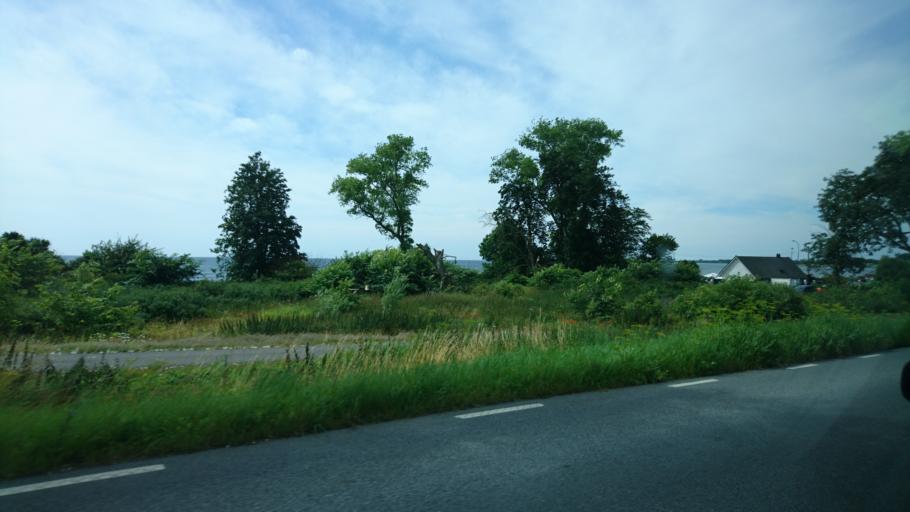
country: SE
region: Skane
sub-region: Skurups Kommun
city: Skivarp
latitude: 55.3864
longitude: 13.5501
